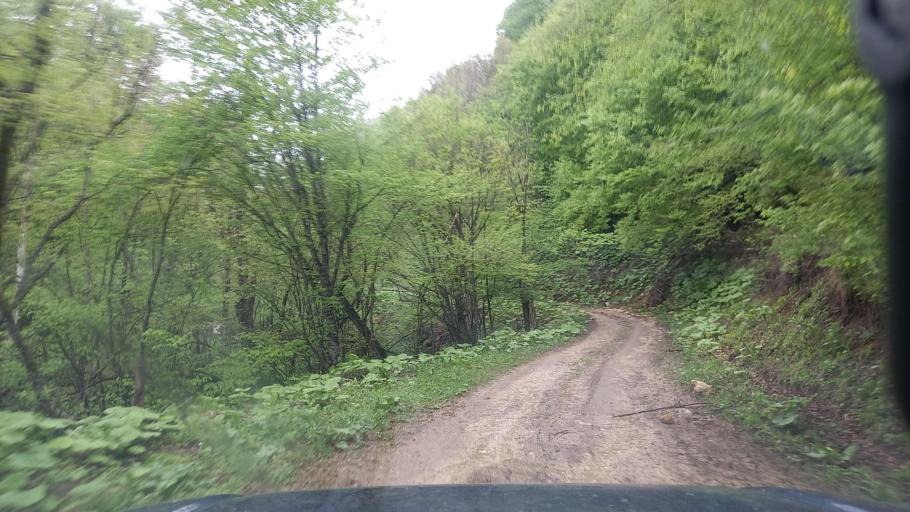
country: RU
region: Kabardino-Balkariya
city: Babugent
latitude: 43.2153
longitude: 43.5490
